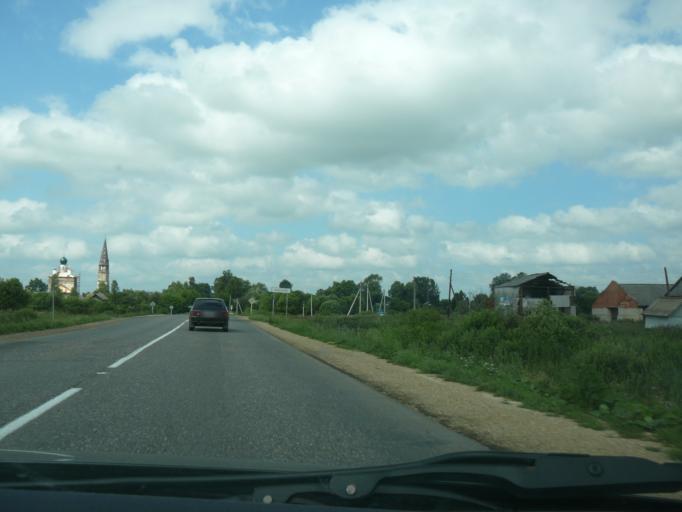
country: RU
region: Jaroslavl
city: Dubki
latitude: 57.2343
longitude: 40.2059
